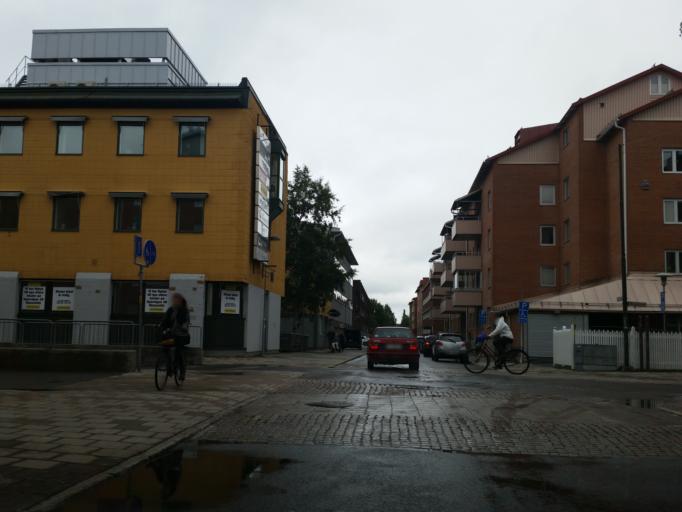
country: SE
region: Vaesterbotten
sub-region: Umea Kommun
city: Umea
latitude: 63.8282
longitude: 20.2595
